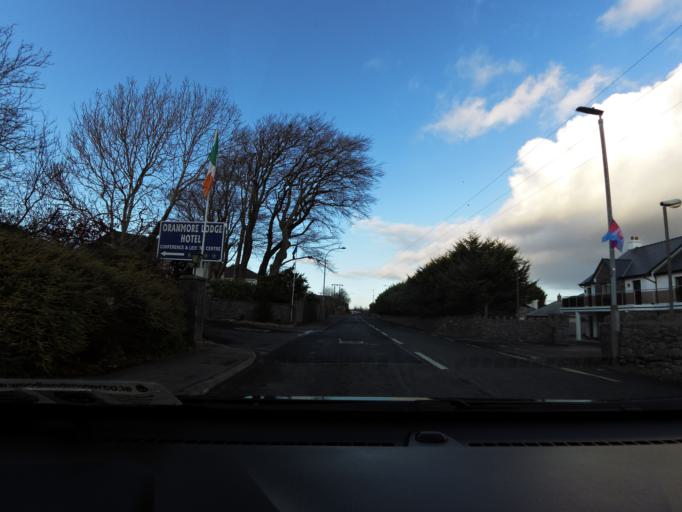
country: IE
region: Connaught
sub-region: County Galway
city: Oranmore
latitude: 53.2747
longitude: -8.9277
